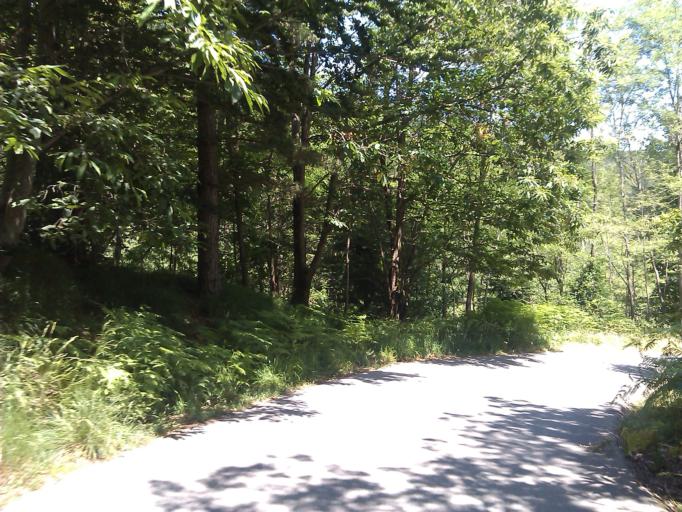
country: IT
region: Tuscany
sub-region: Provincia di Prato
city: Cantagallo
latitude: 43.9881
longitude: 11.0418
